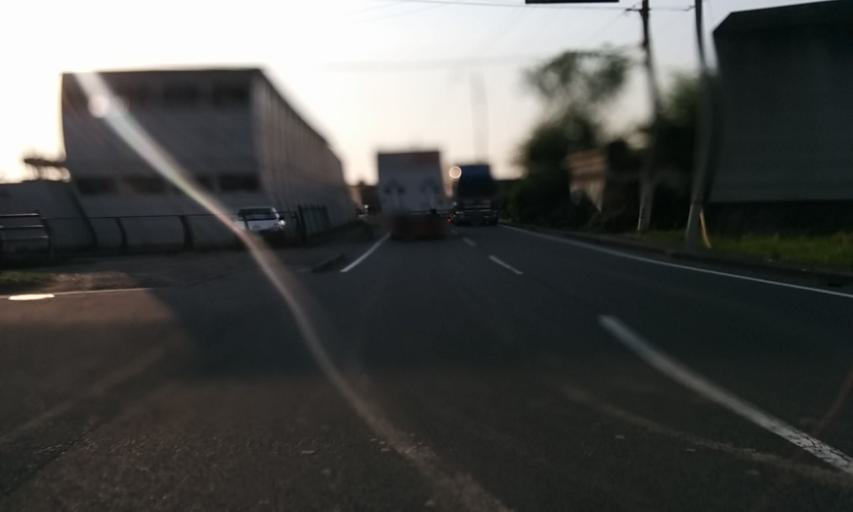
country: JP
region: Ehime
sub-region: Shikoku-chuo Shi
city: Matsuyama
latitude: 33.7769
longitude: 132.8371
